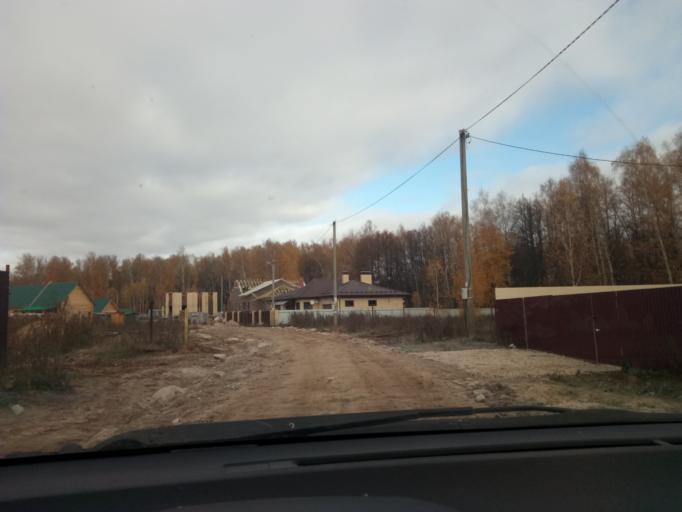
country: RU
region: Tatarstan
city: Staroye Arakchino
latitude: 55.9688
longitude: 49.0453
